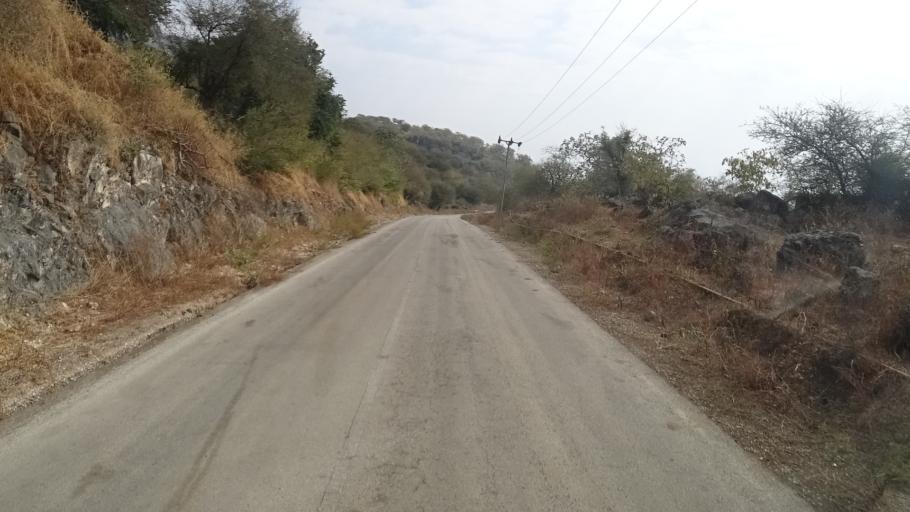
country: YE
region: Al Mahrah
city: Hawf
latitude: 16.7073
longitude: 53.2196
